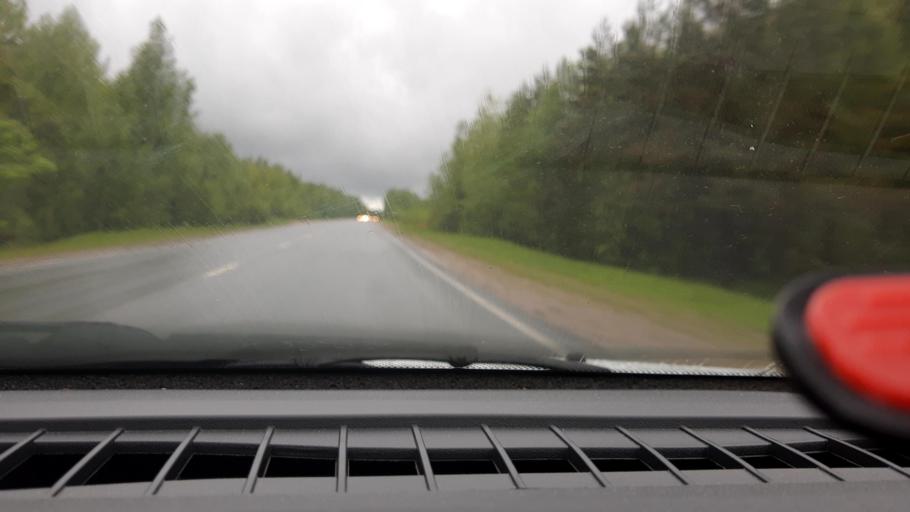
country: RU
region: Nizjnij Novgorod
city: Semenov
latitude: 56.7823
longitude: 44.4362
